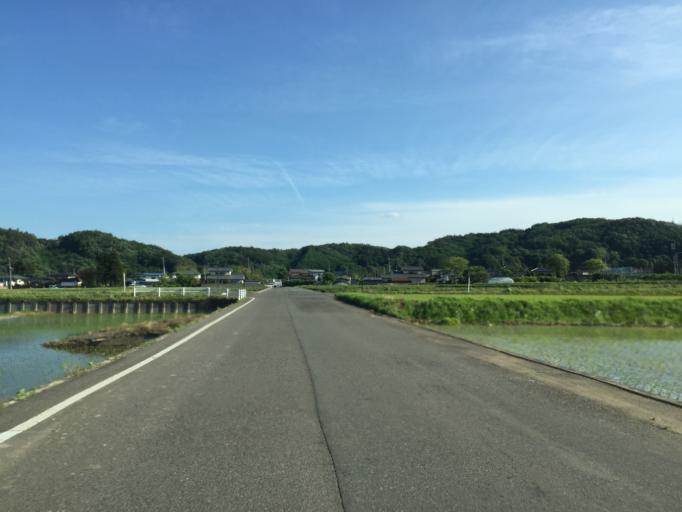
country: JP
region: Fukushima
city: Fukushima-shi
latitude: 37.7314
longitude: 140.4192
